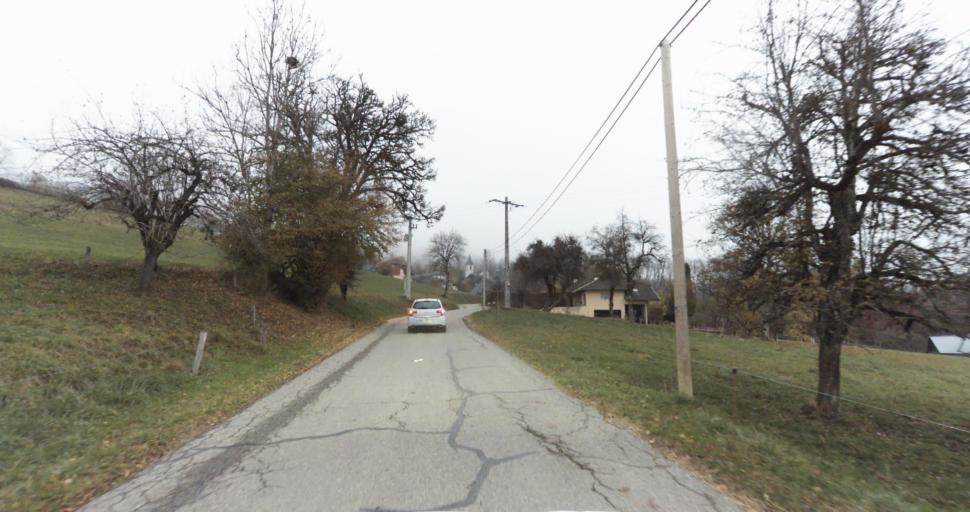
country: FR
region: Rhone-Alpes
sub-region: Departement de la Haute-Savoie
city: Saint-Jorioz
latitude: 45.7813
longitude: 6.1478
